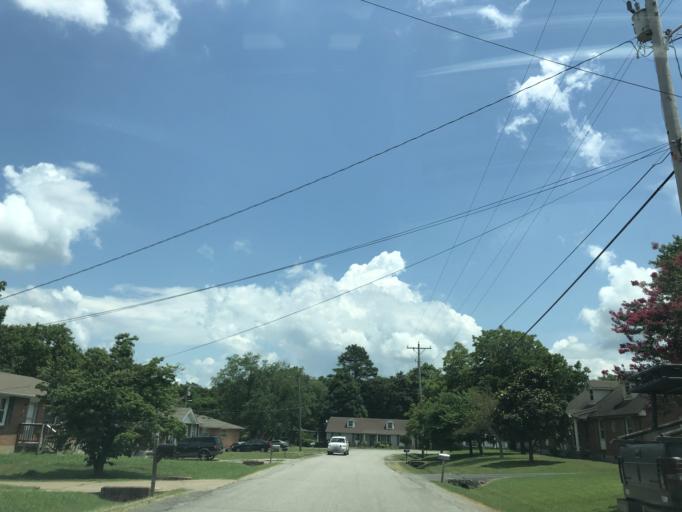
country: US
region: Tennessee
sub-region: Davidson County
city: Lakewood
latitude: 36.2013
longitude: -86.6255
